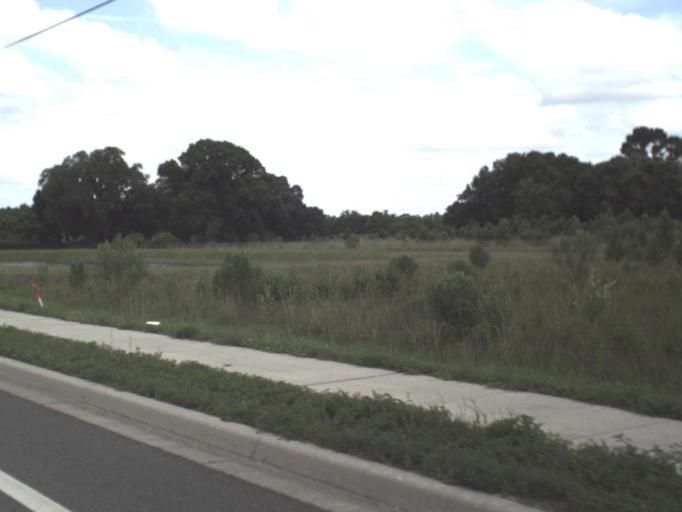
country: US
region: Florida
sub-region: Nassau County
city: Callahan
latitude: 30.5857
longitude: -81.8001
